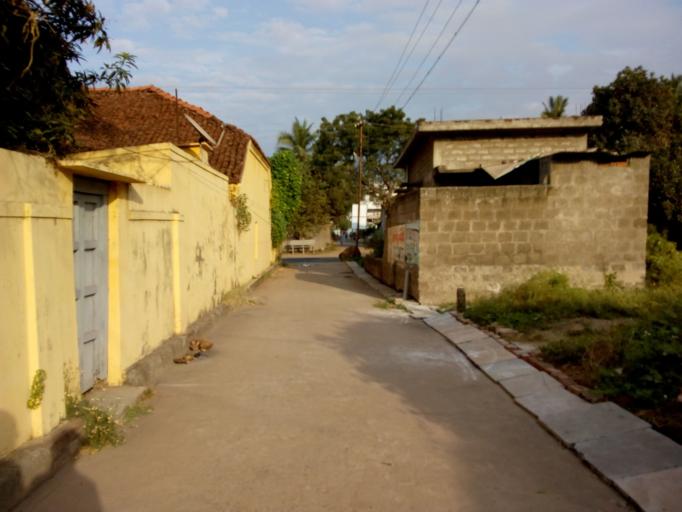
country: IN
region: Andhra Pradesh
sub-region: West Godavari
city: Nidadavole
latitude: 16.9361
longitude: 81.6707
